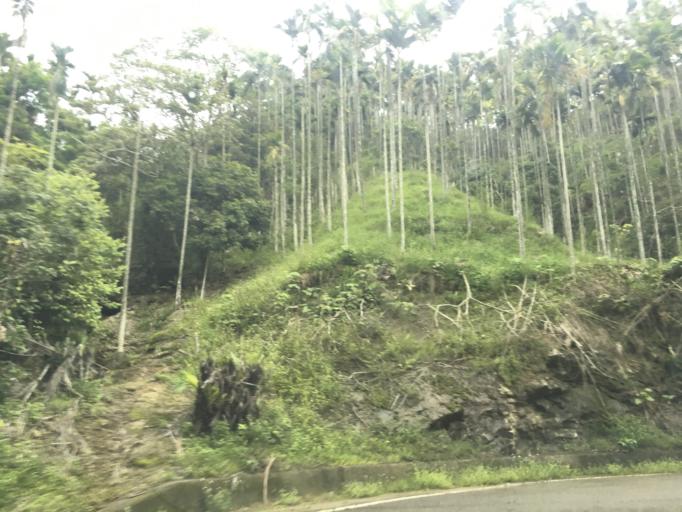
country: TW
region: Taiwan
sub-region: Yunlin
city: Douliu
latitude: 23.5667
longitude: 120.6280
